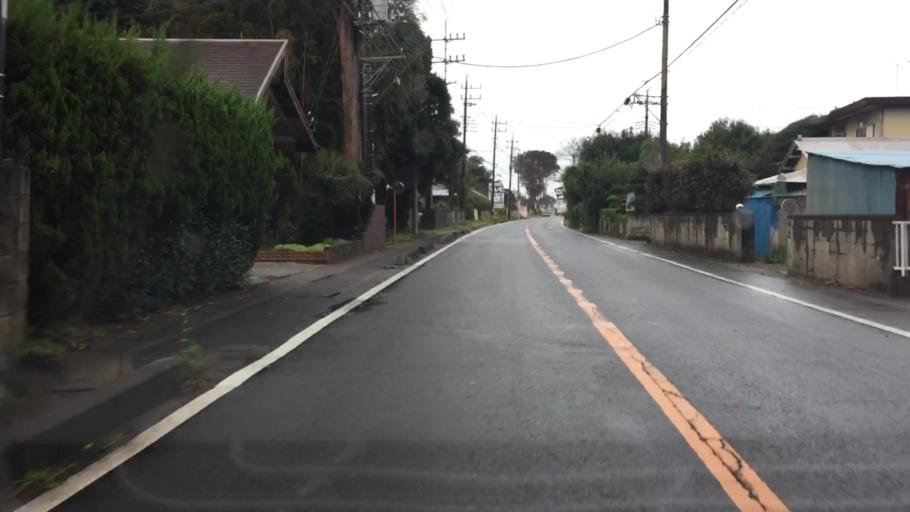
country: JP
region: Ibaraki
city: Toride
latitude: 35.8618
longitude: 140.1179
